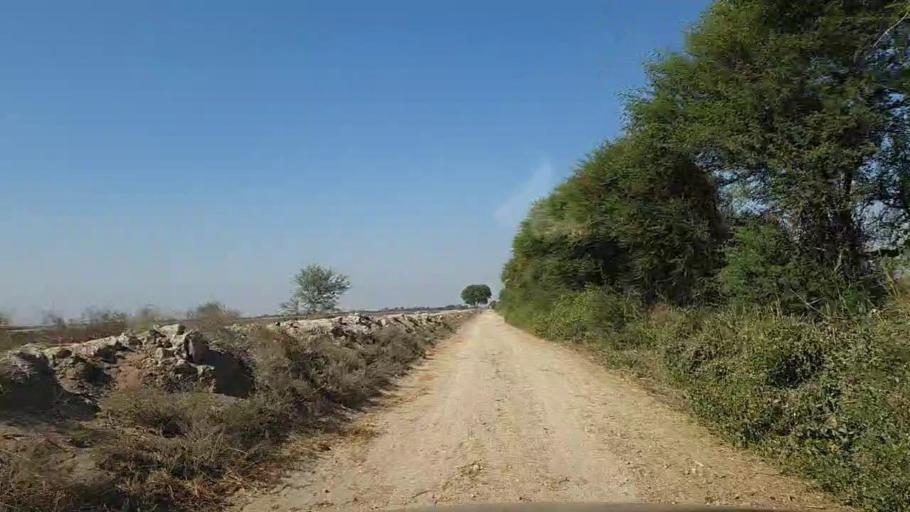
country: PK
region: Sindh
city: Mirpur Batoro
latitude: 24.7202
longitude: 68.2348
